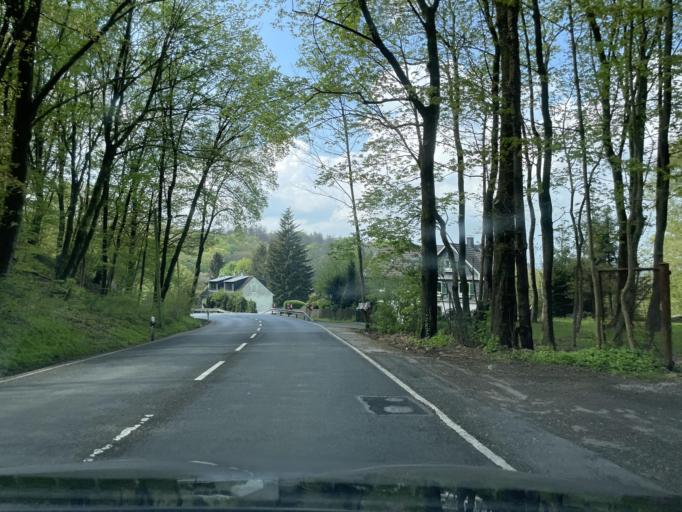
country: DE
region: North Rhine-Westphalia
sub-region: Regierungsbezirk Dusseldorf
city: Wuppertal
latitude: 51.2490
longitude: 7.1829
